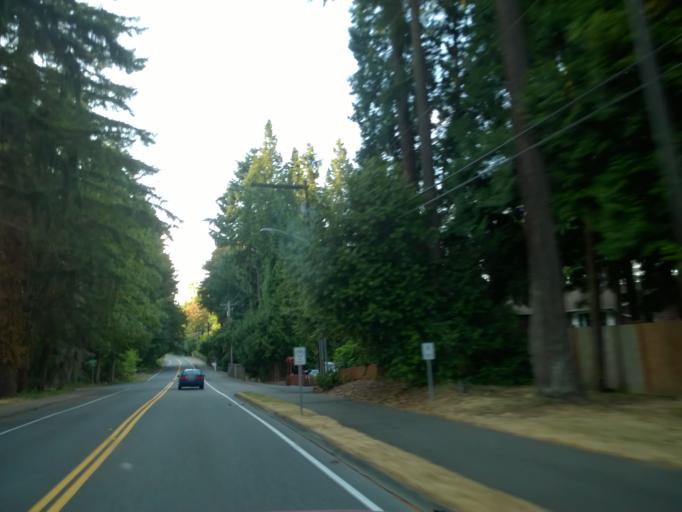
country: US
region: Washington
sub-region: King County
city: Woodinville
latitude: 47.7640
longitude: -122.1636
